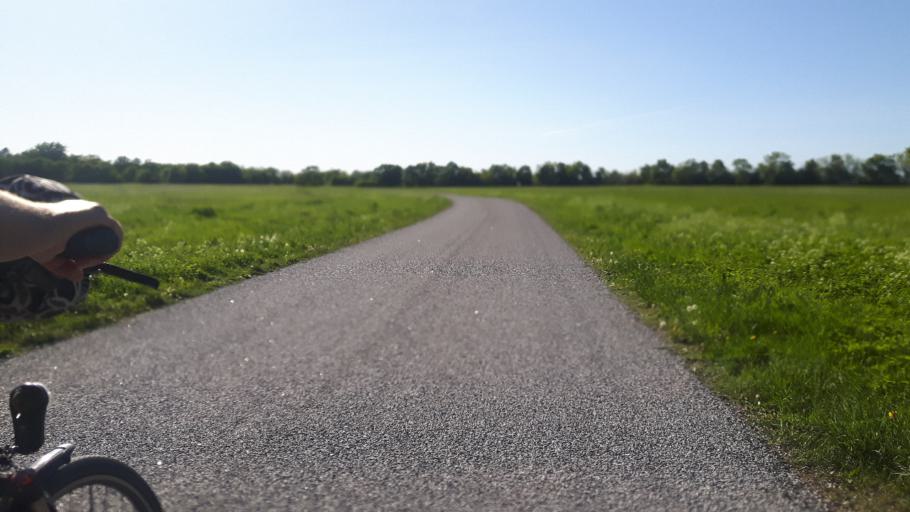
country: EE
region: Ida-Virumaa
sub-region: Kohtla-Jaerve linn
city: Kohtla-Jarve
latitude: 59.4381
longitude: 27.1943
